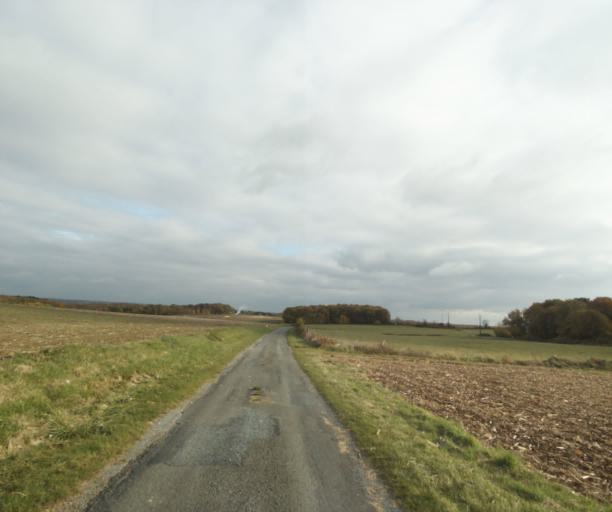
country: FR
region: Poitou-Charentes
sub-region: Departement de la Charente-Maritime
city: Saint-Georges-des-Coteaux
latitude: 45.7642
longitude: -0.6828
